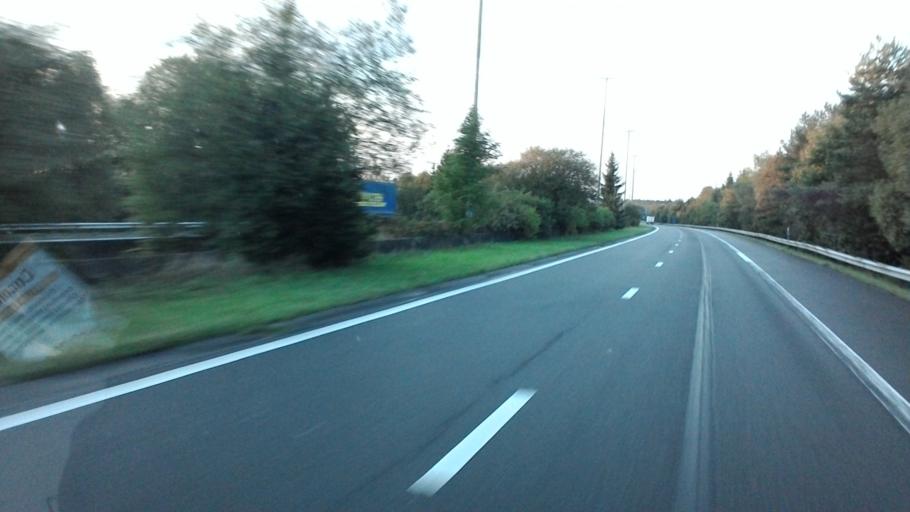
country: BE
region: Wallonia
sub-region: Province de Liege
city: Aywaille
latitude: 50.4153
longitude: 5.7072
